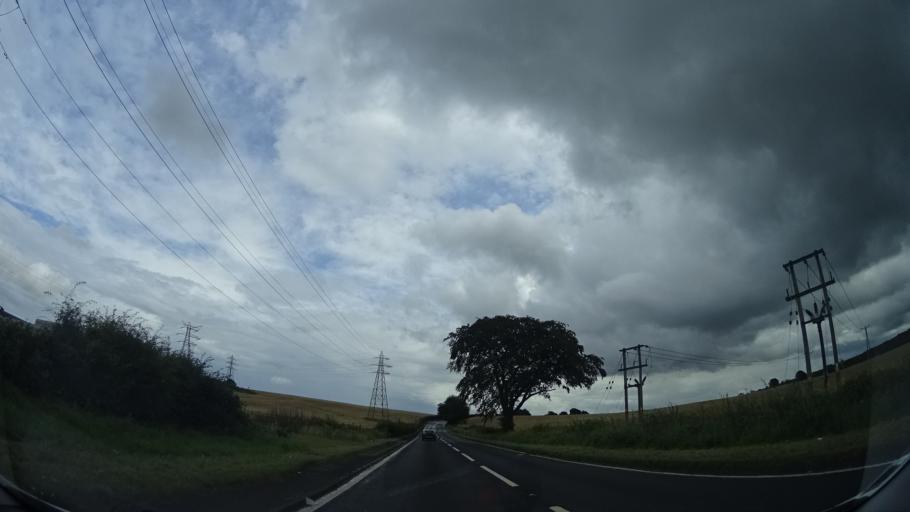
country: GB
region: Scotland
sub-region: Falkirk
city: Bonnybridge
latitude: 56.0066
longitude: -3.8590
